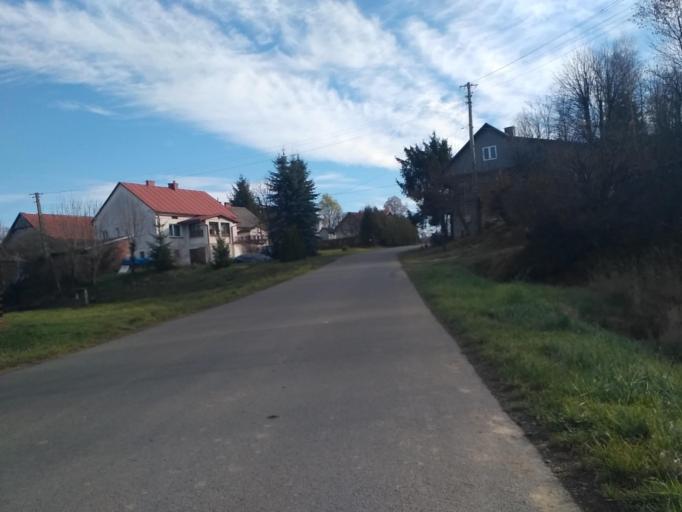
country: PL
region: Subcarpathian Voivodeship
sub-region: Powiat brzozowski
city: Blizne
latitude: 49.7341
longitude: 21.9828
